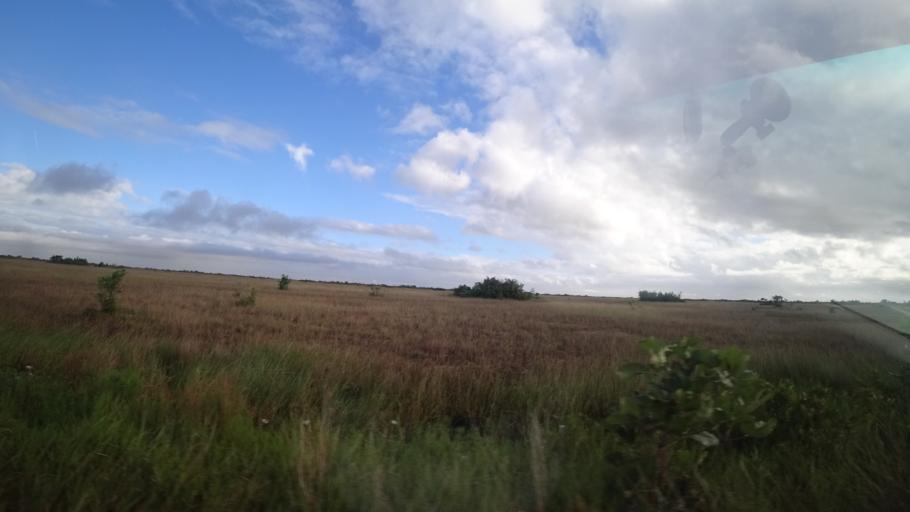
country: MZ
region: Sofala
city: Beira
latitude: -19.6965
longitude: 35.0327
